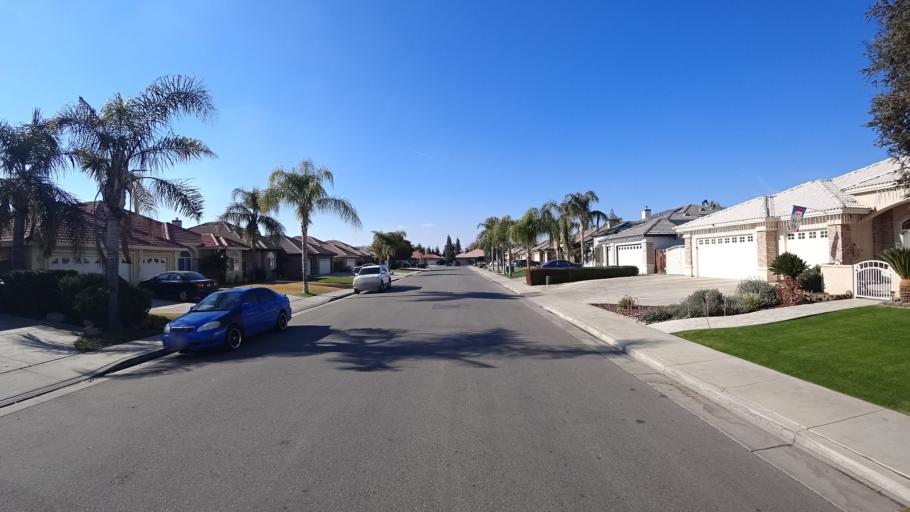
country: US
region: California
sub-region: Kern County
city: Greenfield
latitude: 35.2901
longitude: -119.0411
